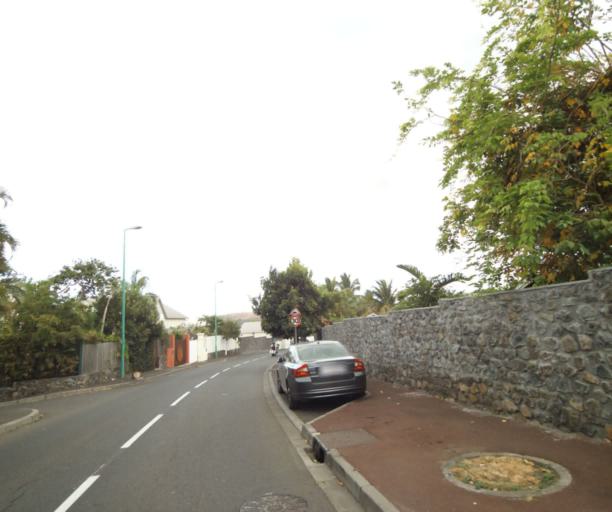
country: RE
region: Reunion
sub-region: Reunion
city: Saint-Paul
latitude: -21.0600
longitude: 55.2267
